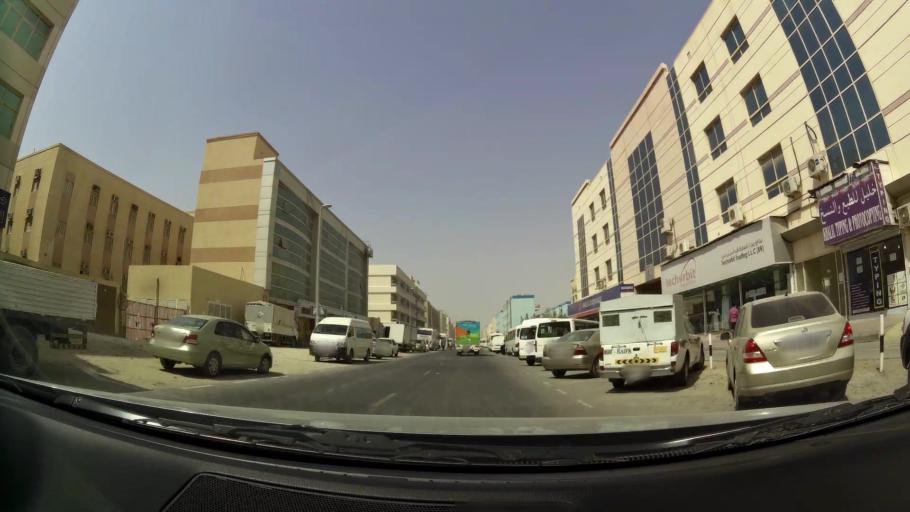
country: AE
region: Dubai
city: Dubai
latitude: 25.1562
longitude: 55.2467
